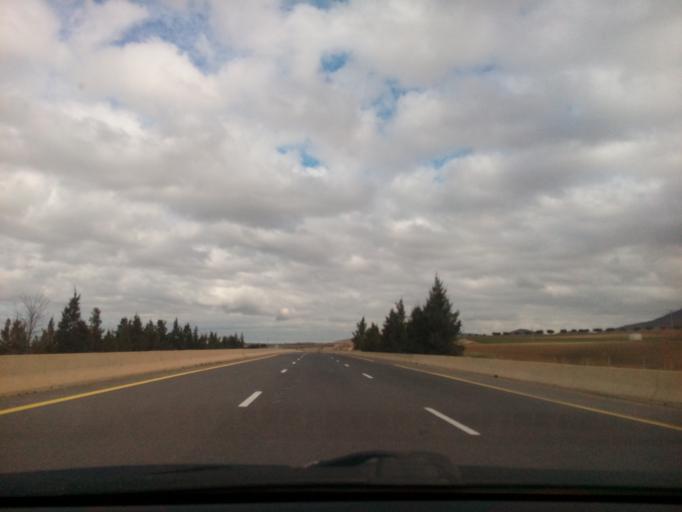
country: DZ
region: Tlemcen
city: Bensekrane
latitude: 35.0001
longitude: -1.1919
